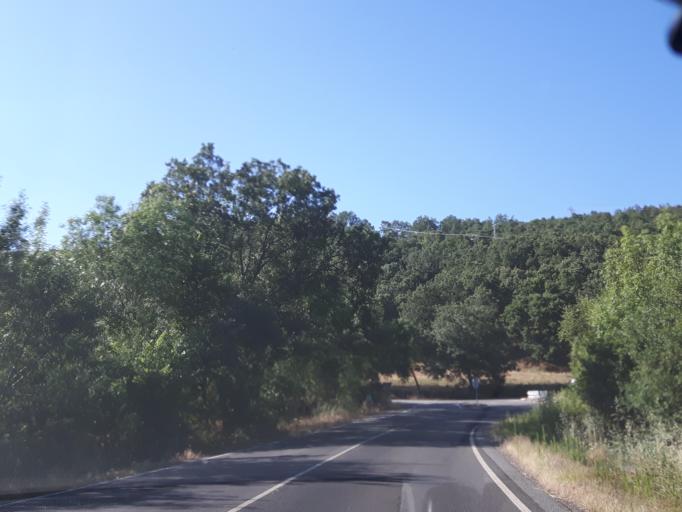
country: ES
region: Castille and Leon
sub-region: Provincia de Salamanca
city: Navalmoral de Bejar
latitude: 40.4151
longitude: -5.7993
